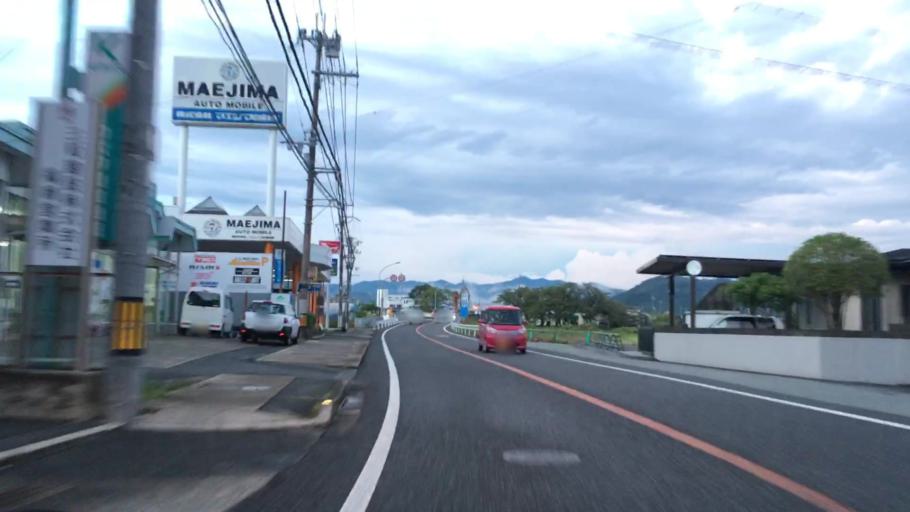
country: JP
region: Hyogo
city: Himeji
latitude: 34.9462
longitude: 134.7476
